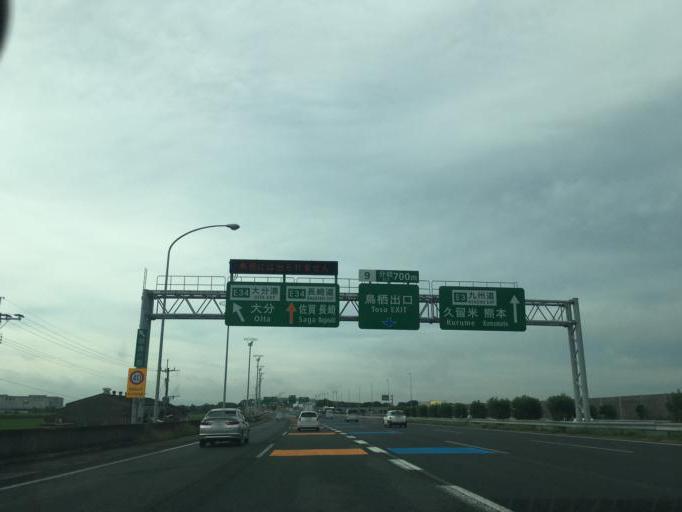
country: JP
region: Saga Prefecture
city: Tosu
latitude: 33.4066
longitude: 130.5377
